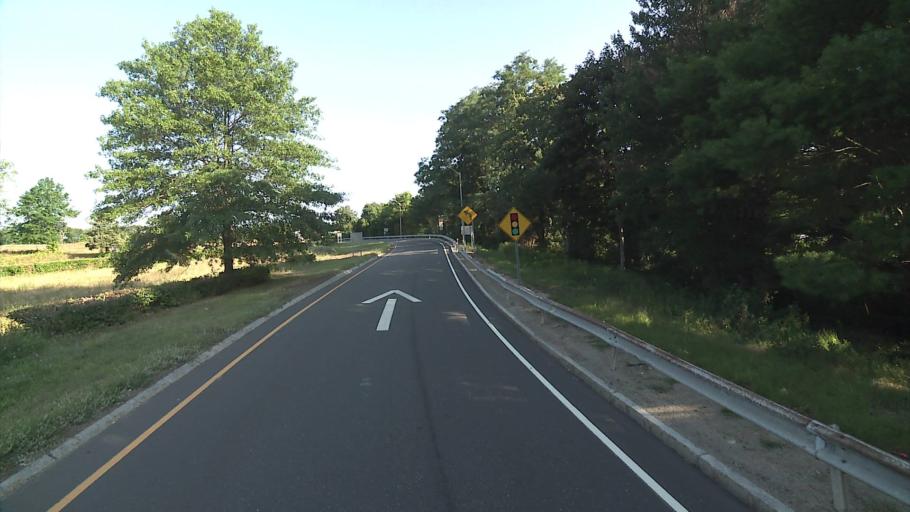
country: US
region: Connecticut
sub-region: New London County
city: New London
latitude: 41.3687
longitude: -72.1136
